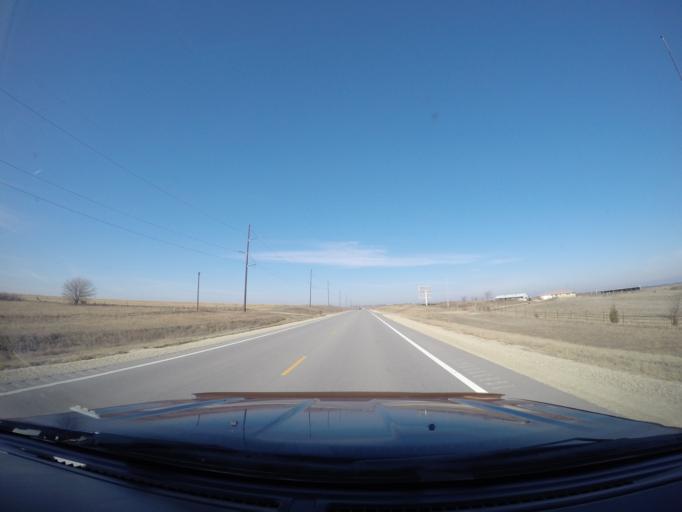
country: US
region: Kansas
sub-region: Riley County
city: Ogden
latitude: 39.2856
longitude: -96.7459
